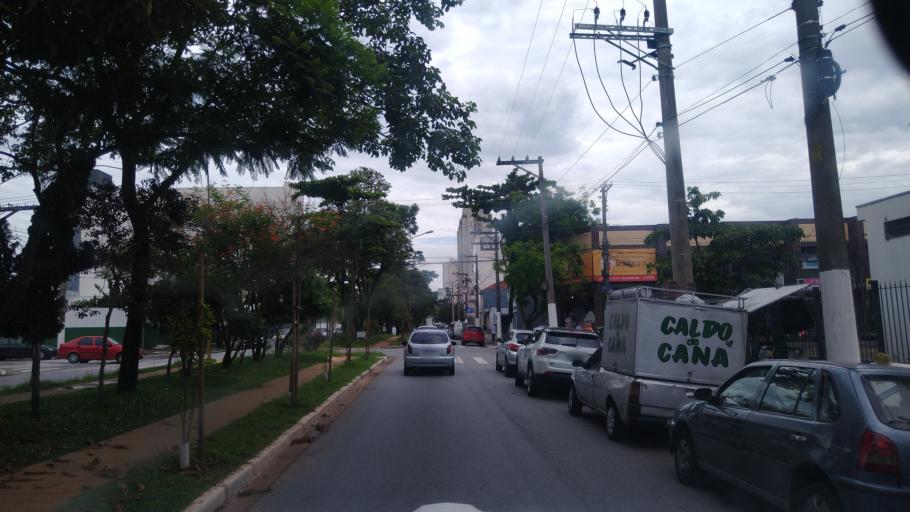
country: BR
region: Sao Paulo
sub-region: Guarulhos
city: Guarulhos
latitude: -23.5159
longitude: -46.5680
